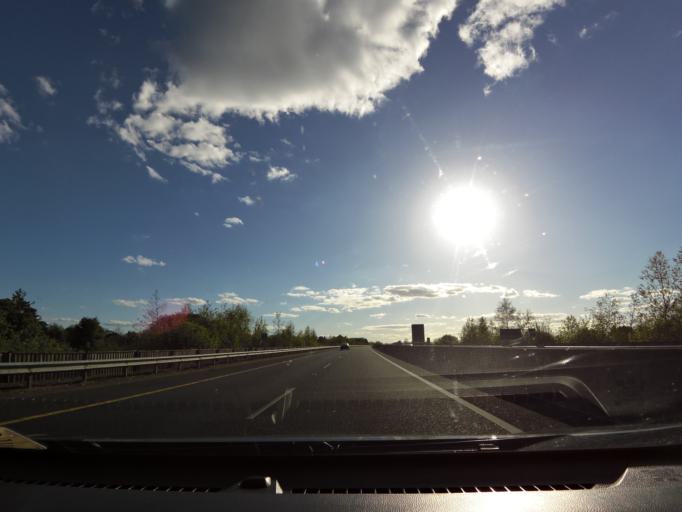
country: IE
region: Connaught
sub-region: County Galway
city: Ballinasloe
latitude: 53.3127
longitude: -8.2571
